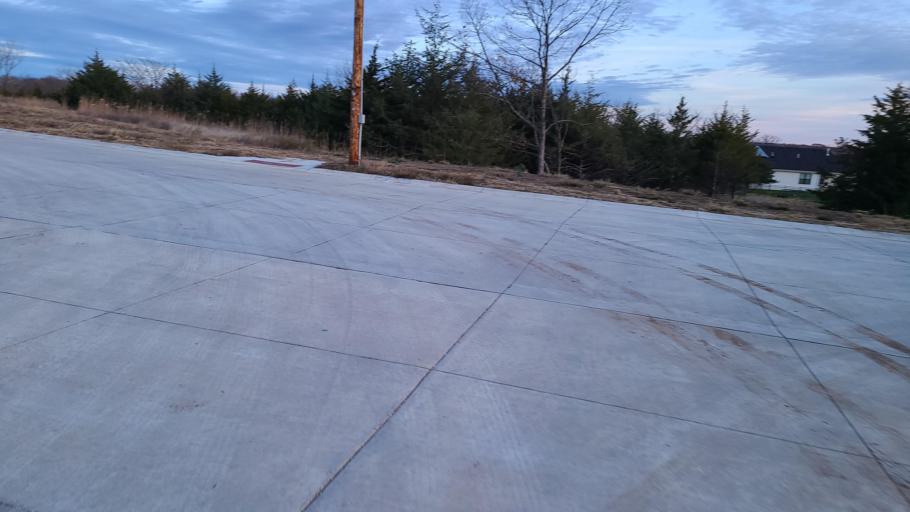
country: US
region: Kansas
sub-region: Riley County
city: Manhattan
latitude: 39.2206
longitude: -96.5094
